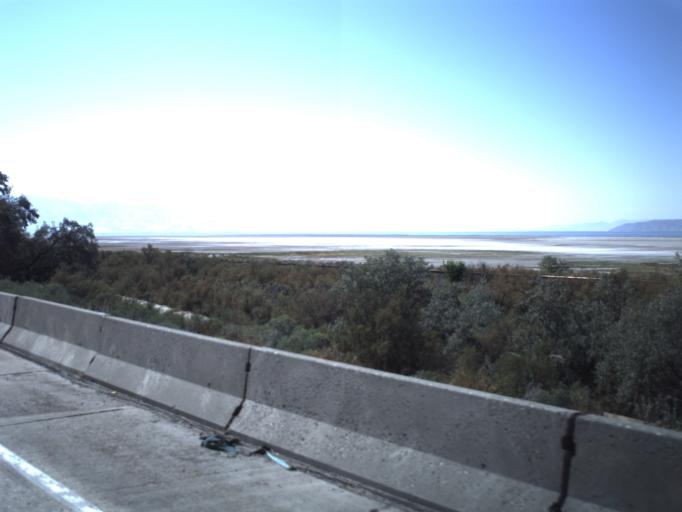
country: US
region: Utah
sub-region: Tooele County
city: Stansbury park
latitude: 40.7167
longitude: -112.2374
